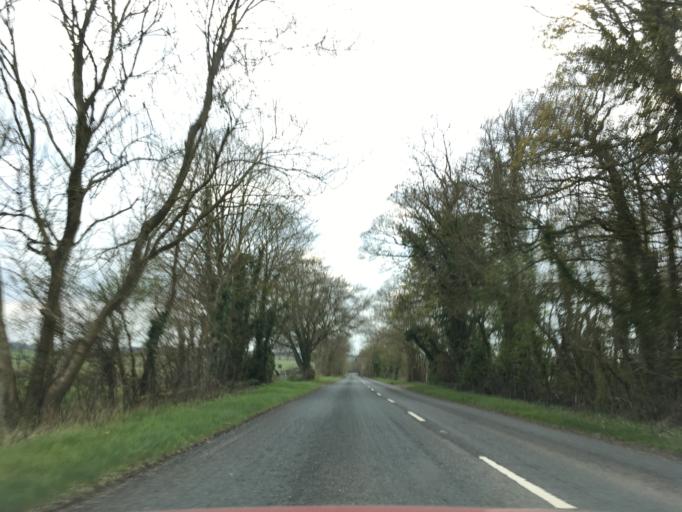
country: GB
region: England
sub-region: Oxfordshire
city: Burford
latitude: 51.7972
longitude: -1.6884
